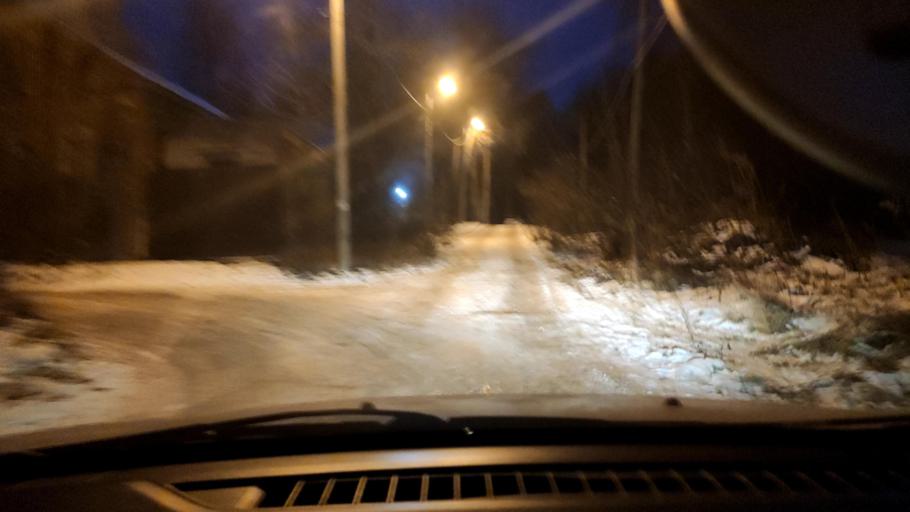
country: RU
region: Perm
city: Kondratovo
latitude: 58.0458
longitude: 56.1111
